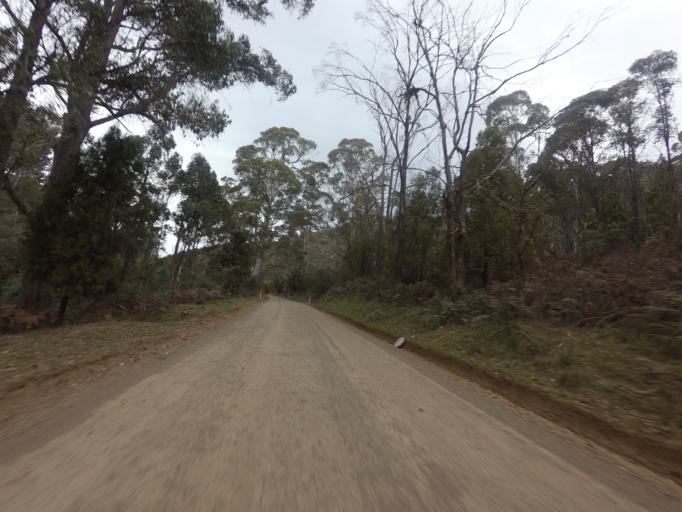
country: AU
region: Tasmania
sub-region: Derwent Valley
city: New Norfolk
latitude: -42.5908
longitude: 147.0268
